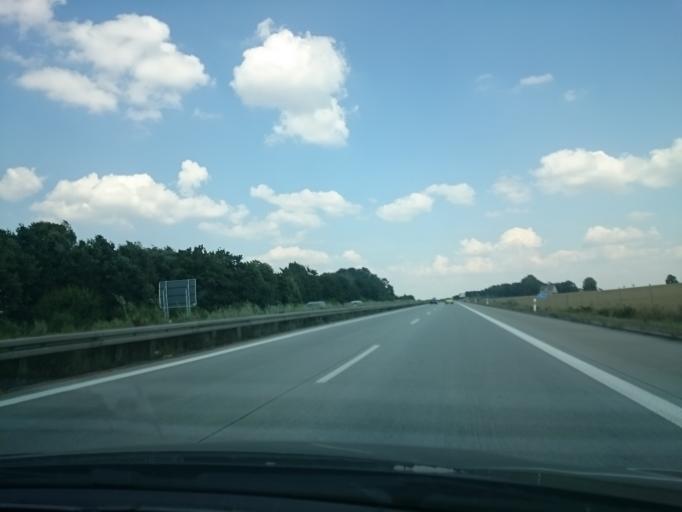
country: DE
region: Saxony
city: Niederdorf
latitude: 50.7531
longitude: 12.8013
